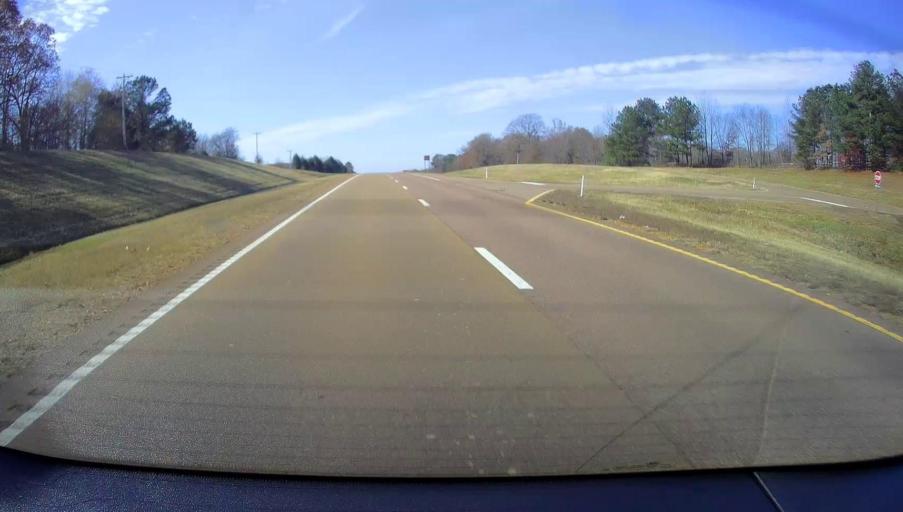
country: US
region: Mississippi
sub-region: Benton County
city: Ashland
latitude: 34.9460
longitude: -89.3466
